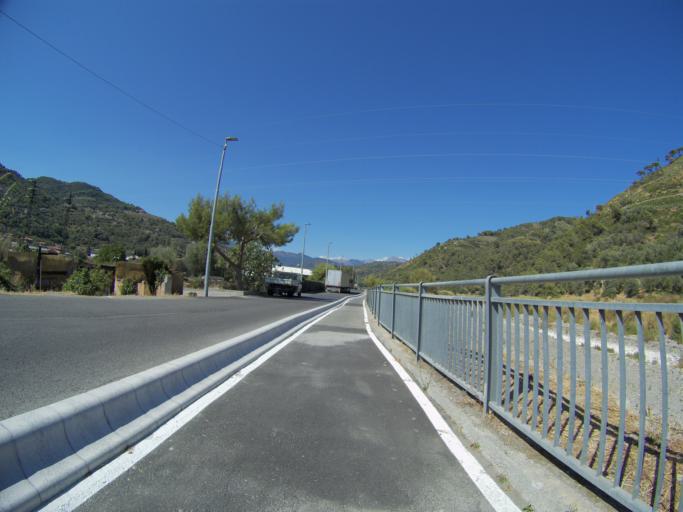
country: IT
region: Liguria
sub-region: Provincia di Imperia
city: Camporosso
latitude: 43.8161
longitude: 7.6327
